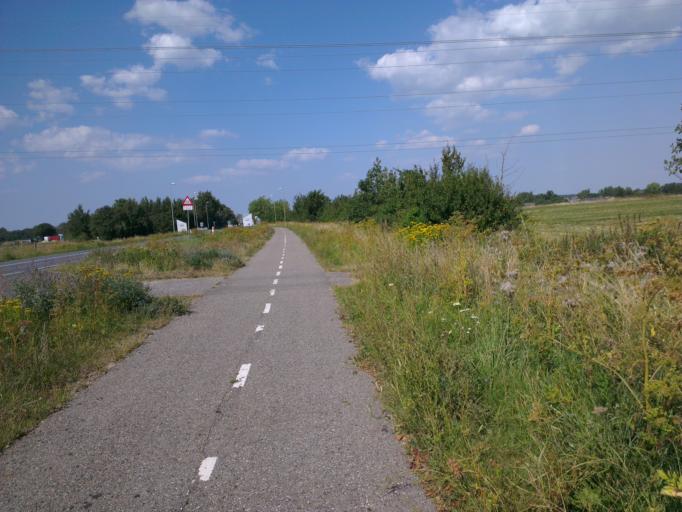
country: DK
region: Capital Region
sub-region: Frederikssund Kommune
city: Skibby
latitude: 55.8012
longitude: 11.9813
